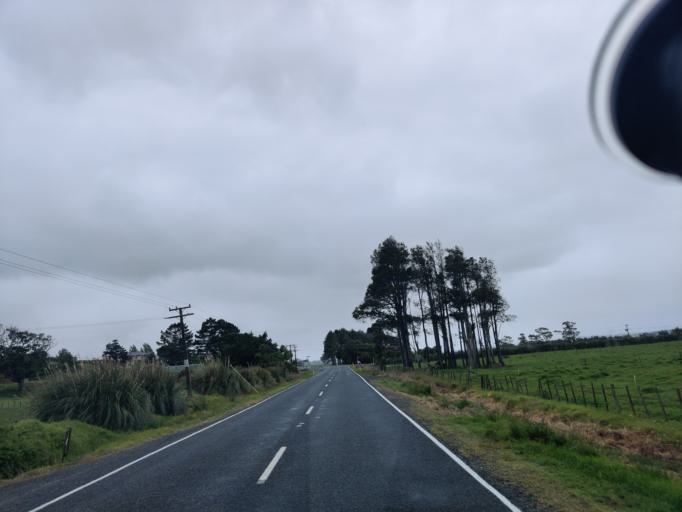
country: NZ
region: Northland
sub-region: Kaipara District
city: Dargaville
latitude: -36.0130
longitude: 173.9317
